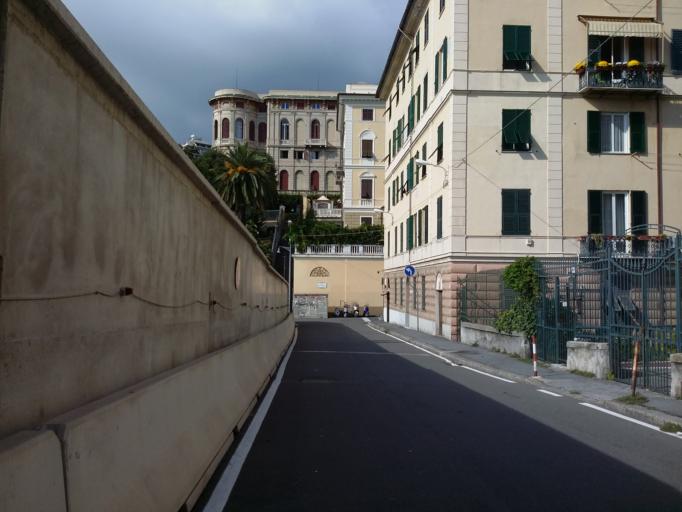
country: IT
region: Liguria
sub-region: Provincia di Genova
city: Genoa
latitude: 44.4090
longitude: 8.9458
